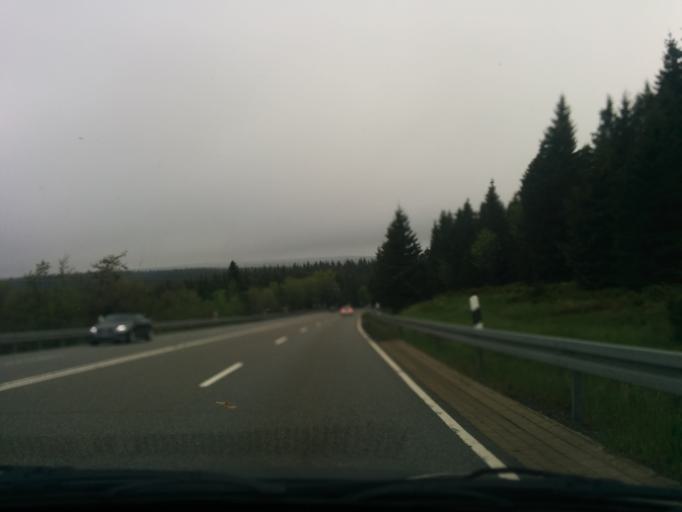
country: DE
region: Lower Saxony
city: Bad Harzburg
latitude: 51.8105
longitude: 10.5258
